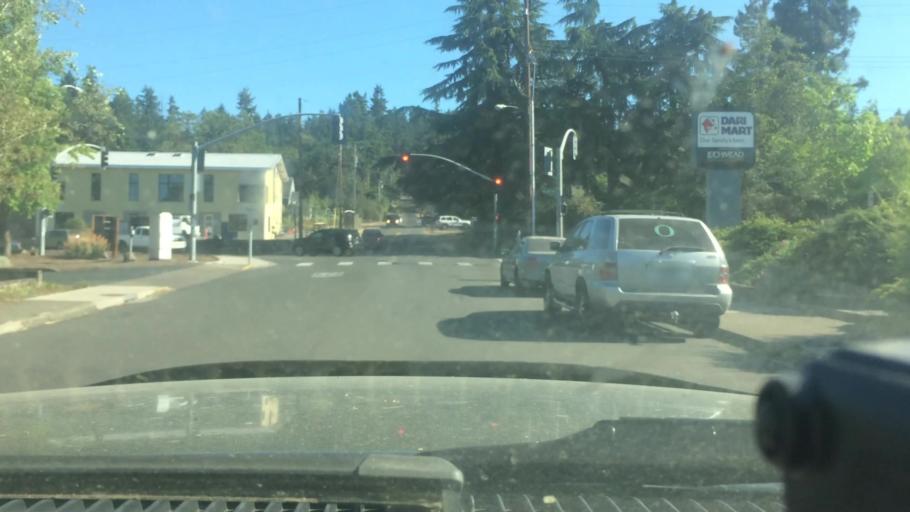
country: US
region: Oregon
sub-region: Lane County
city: Eugene
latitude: 44.0281
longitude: -123.1056
